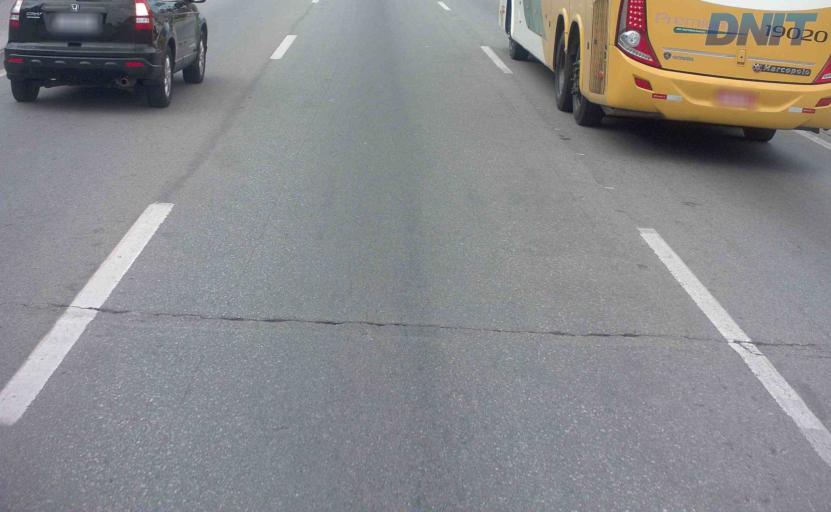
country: BR
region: Minas Gerais
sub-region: Belo Horizonte
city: Belo Horizonte
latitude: -19.8578
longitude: -43.9046
